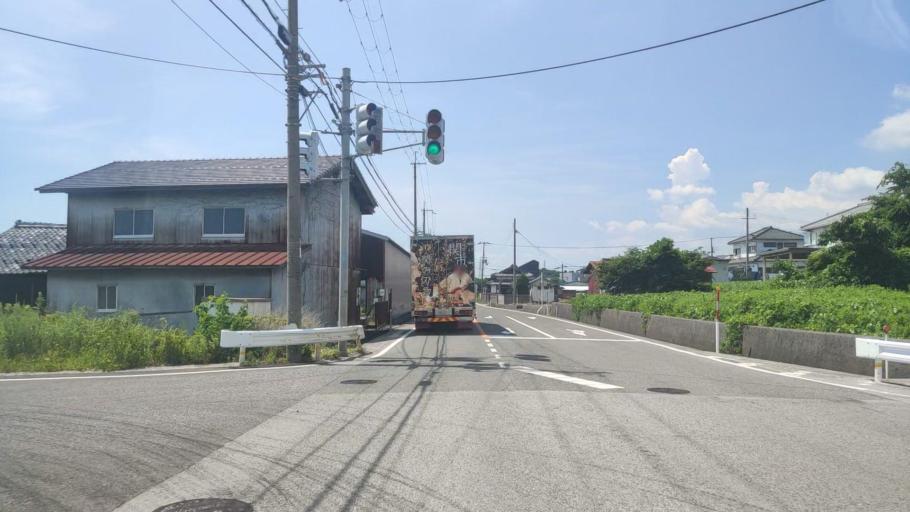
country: JP
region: Shiga Prefecture
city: Nagahama
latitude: 35.3807
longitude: 136.3743
